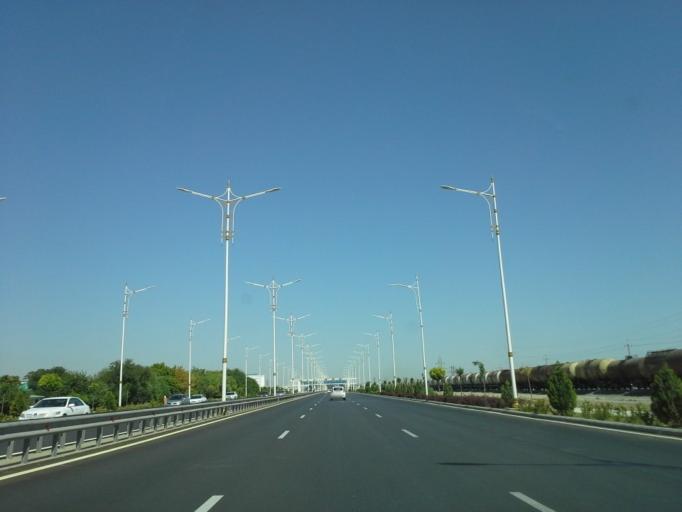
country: TM
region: Ahal
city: Ashgabat
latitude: 37.9718
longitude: 58.3504
